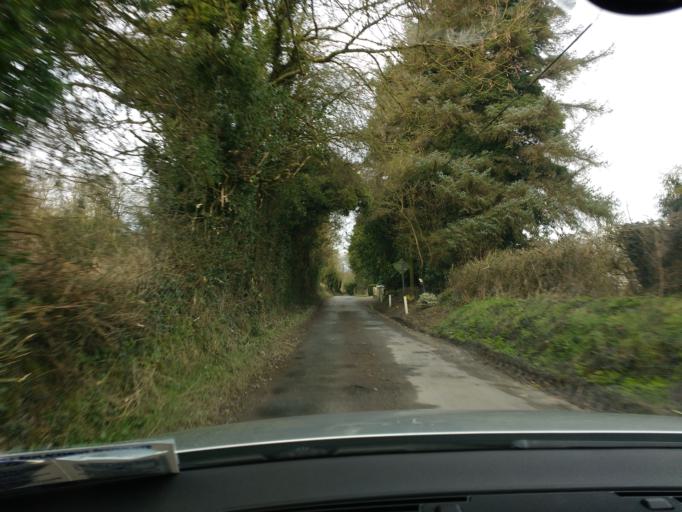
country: IE
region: Leinster
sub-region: Kilkenny
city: Callan
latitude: 52.6580
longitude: -7.5513
